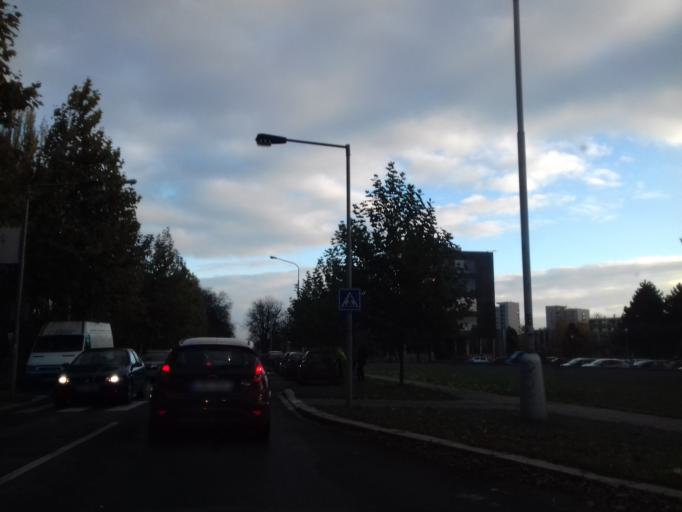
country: CZ
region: Olomoucky
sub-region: Okres Olomouc
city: Olomouc
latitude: 49.5907
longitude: 17.2613
